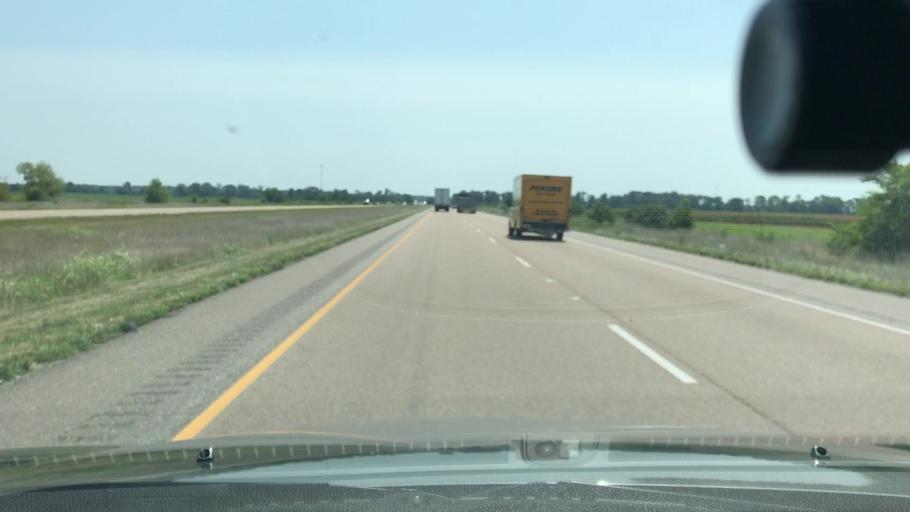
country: US
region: Illinois
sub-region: Washington County
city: Okawville
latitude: 38.4237
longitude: -89.4567
